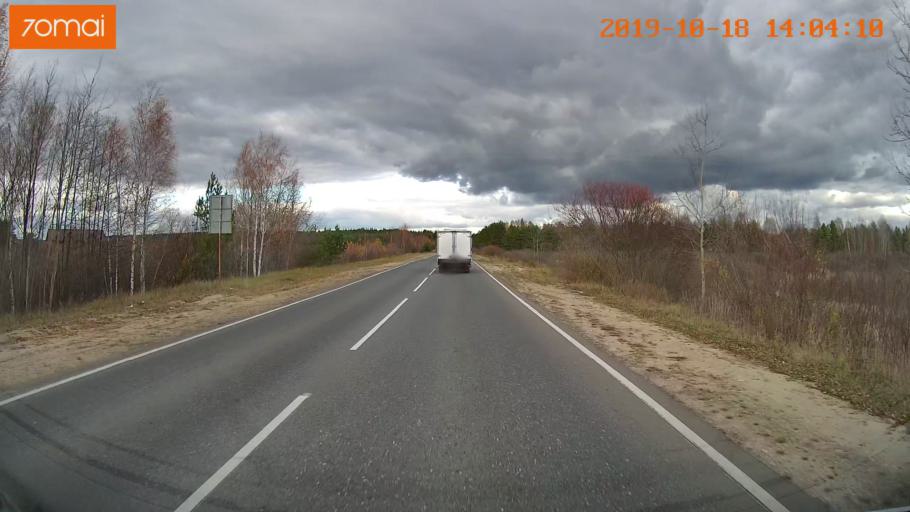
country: RU
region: Rjazan
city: Spas-Klepiki
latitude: 55.1229
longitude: 40.1335
